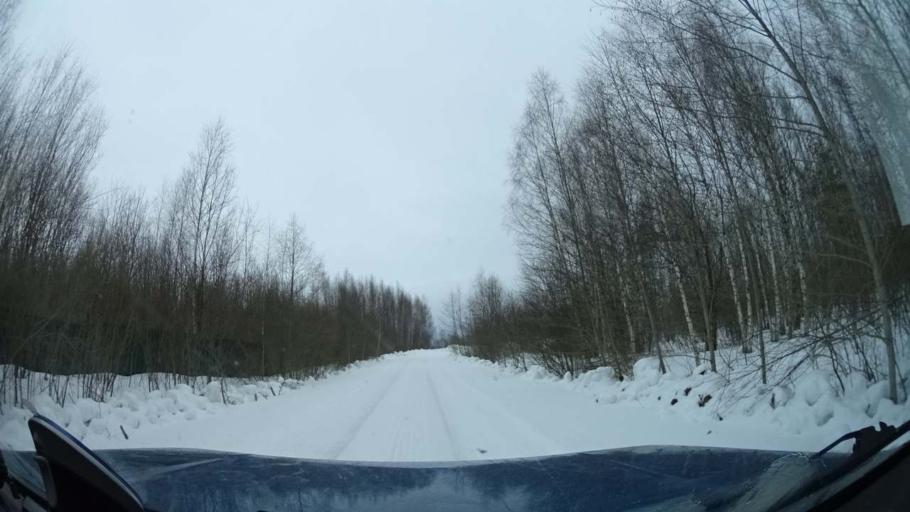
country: RU
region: Tverskaya
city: Gorodnya
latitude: 56.7469
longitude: 36.3550
